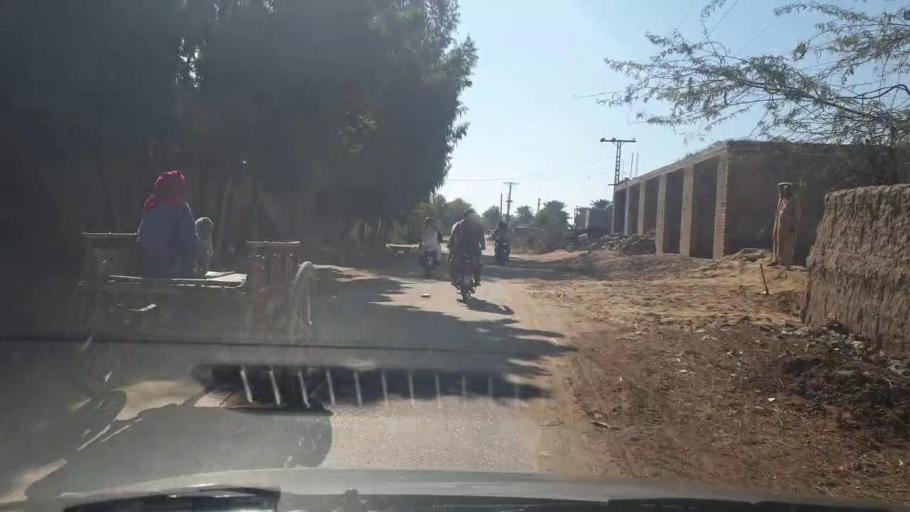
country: PK
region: Sindh
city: Bozdar
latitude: 27.0928
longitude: 68.6248
